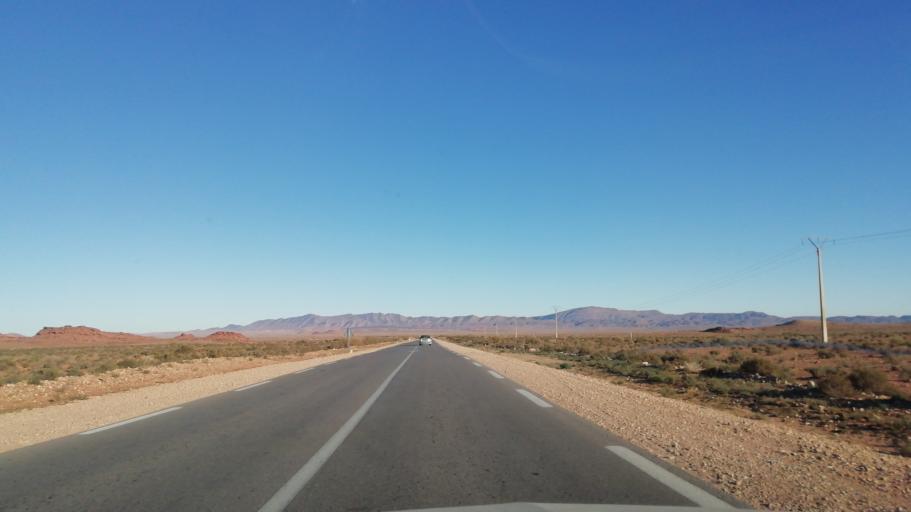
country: DZ
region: El Bayadh
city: El Abiodh Sidi Cheikh
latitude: 33.1705
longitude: 0.4947
